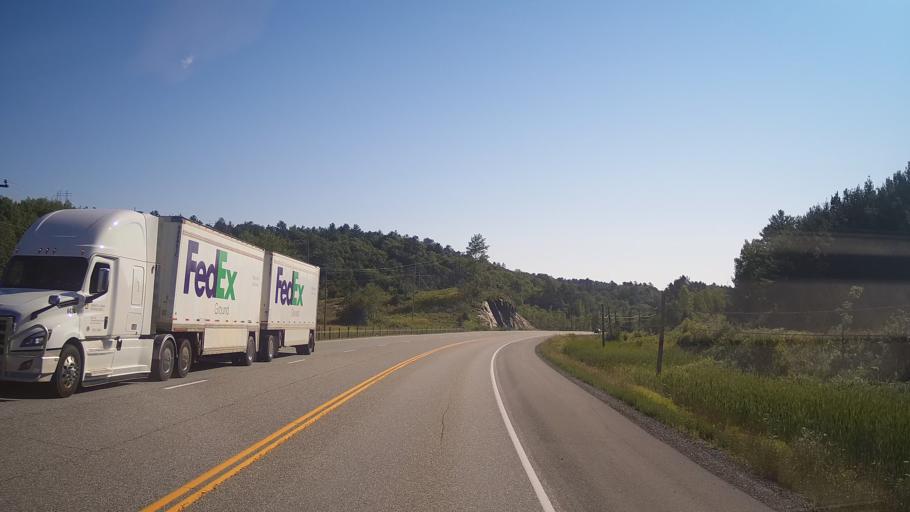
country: CA
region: Ontario
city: Elliot Lake
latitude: 46.2059
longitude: -82.6820
